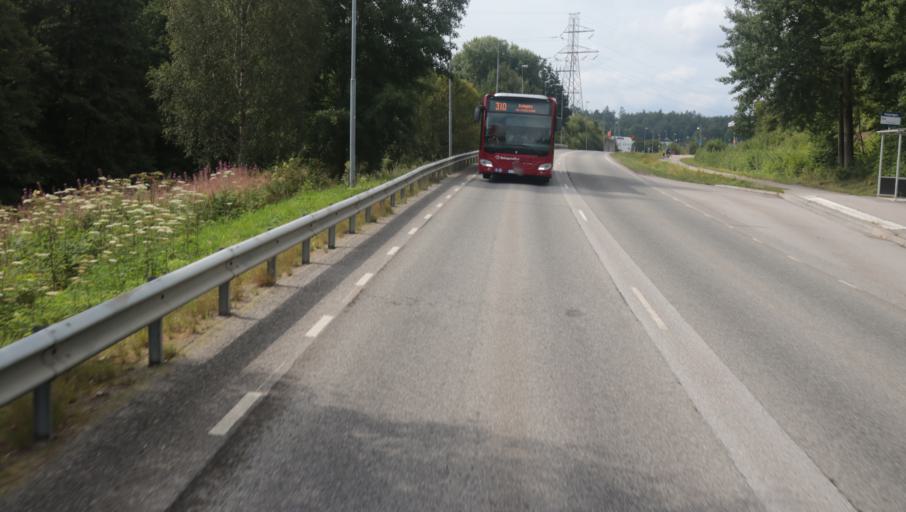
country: SE
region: Blekinge
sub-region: Karlshamns Kommun
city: Karlshamn
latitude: 56.1979
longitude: 14.8482
